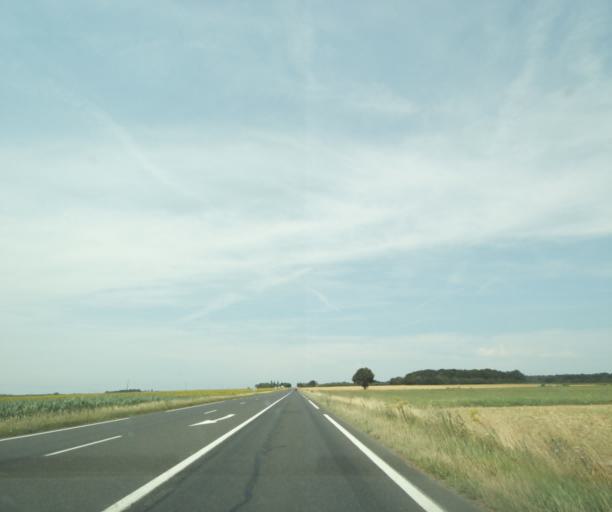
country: FR
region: Centre
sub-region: Departement d'Indre-et-Loire
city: Sainte-Maure-de-Touraine
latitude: 47.1645
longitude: 0.6502
